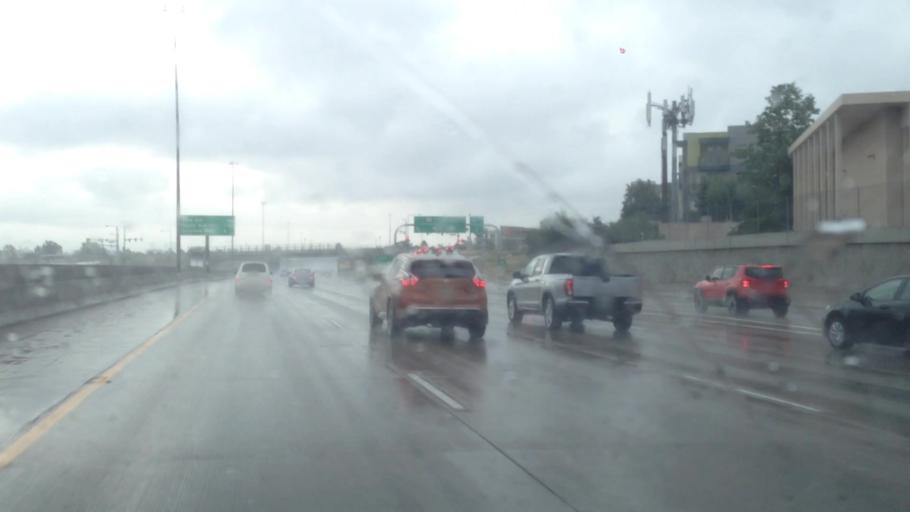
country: US
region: Colorado
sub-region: Arapahoe County
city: Cherry Hills Village
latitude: 39.6504
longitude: -104.9166
